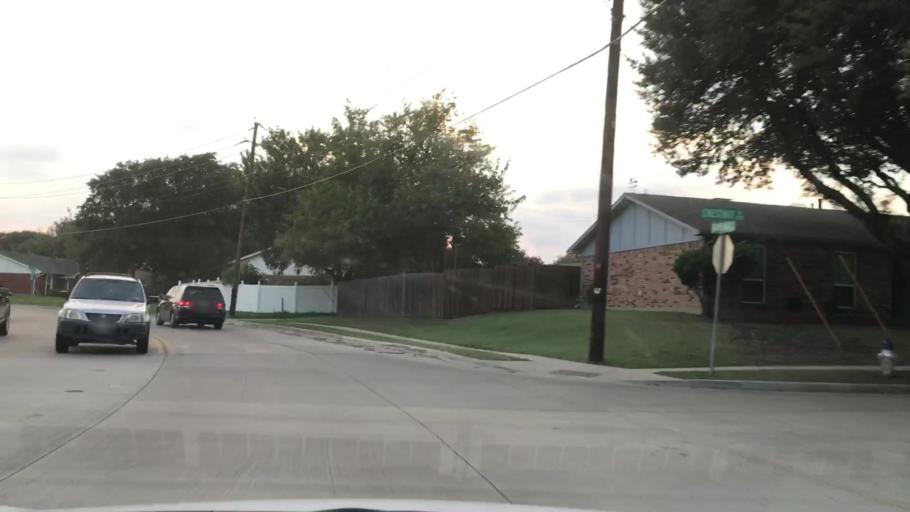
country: US
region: Texas
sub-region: Dallas County
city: Carrollton
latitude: 33.0014
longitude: -96.8778
